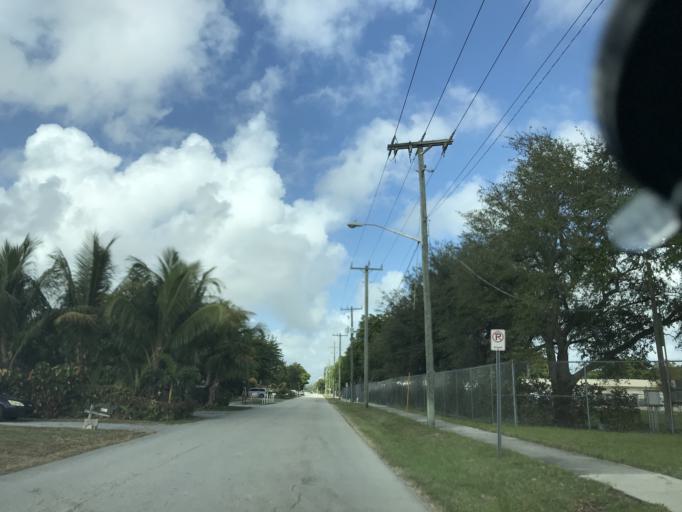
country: US
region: Florida
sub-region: Palm Beach County
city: Delray Beach
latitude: 26.4519
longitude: -80.0770
